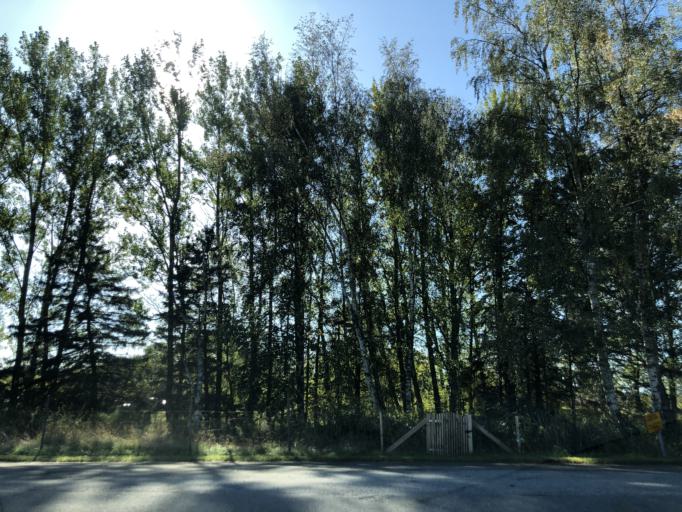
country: SE
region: Vaestra Goetaland
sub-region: Goteborg
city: Majorna
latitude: 57.7750
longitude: 11.9100
